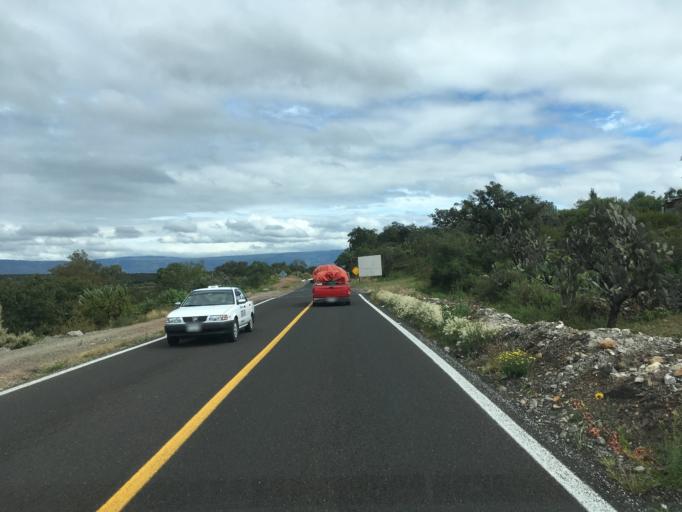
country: MX
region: Hidalgo
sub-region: Atotonilco el Grande
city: Santa Maria Amajac
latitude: 20.4081
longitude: -98.7072
